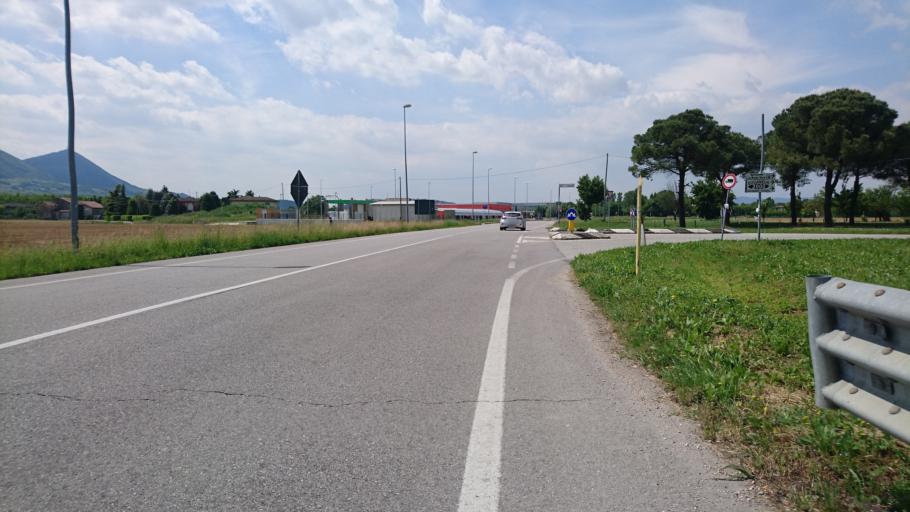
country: IT
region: Veneto
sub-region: Provincia di Padova
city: Montemerlo
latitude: 45.3890
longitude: 11.7108
